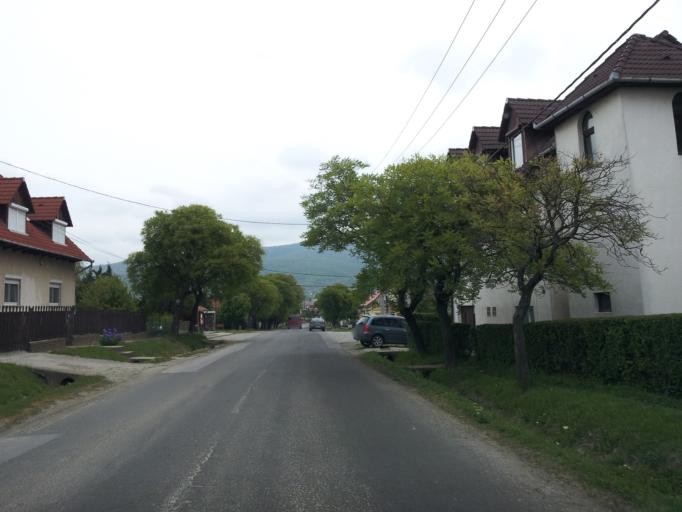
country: HU
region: Baranya
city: Hosszuheteny
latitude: 46.1502
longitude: 18.3547
